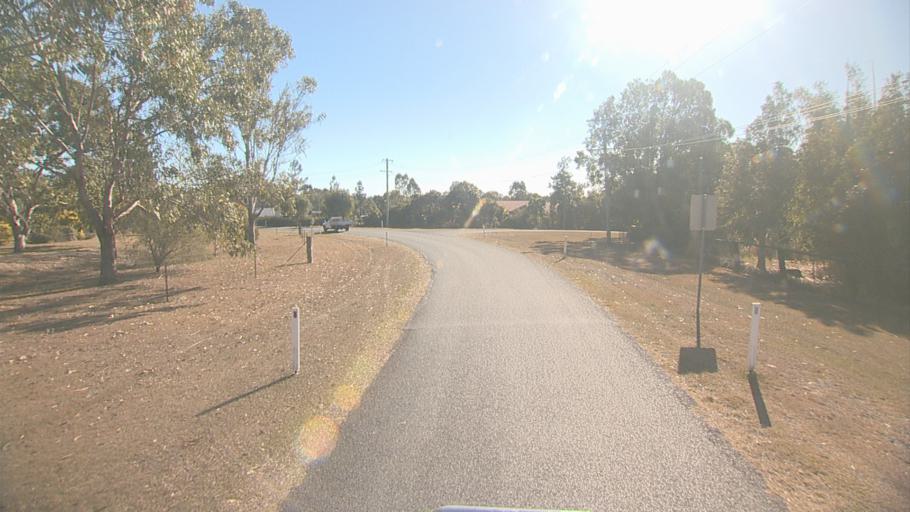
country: AU
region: Queensland
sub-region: Logan
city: North Maclean
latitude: -27.7873
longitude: 153.0063
